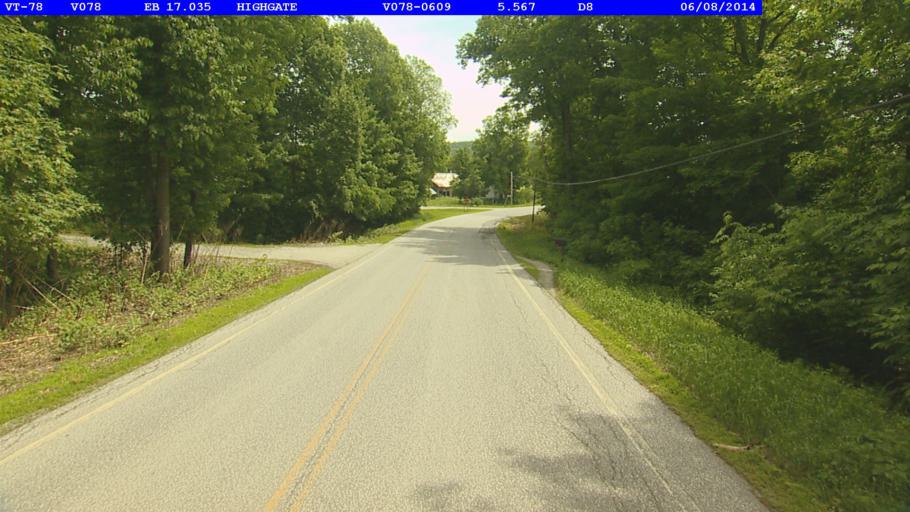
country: US
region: Vermont
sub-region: Franklin County
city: Swanton
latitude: 44.9394
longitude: -73.0005
